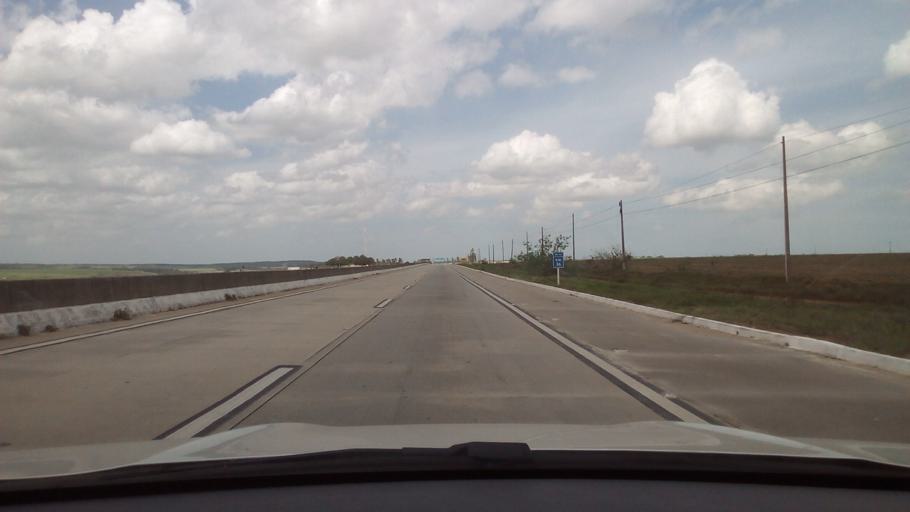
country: BR
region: Paraiba
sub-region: Mamanguape
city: Mamanguape
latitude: -6.8032
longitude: -35.1399
